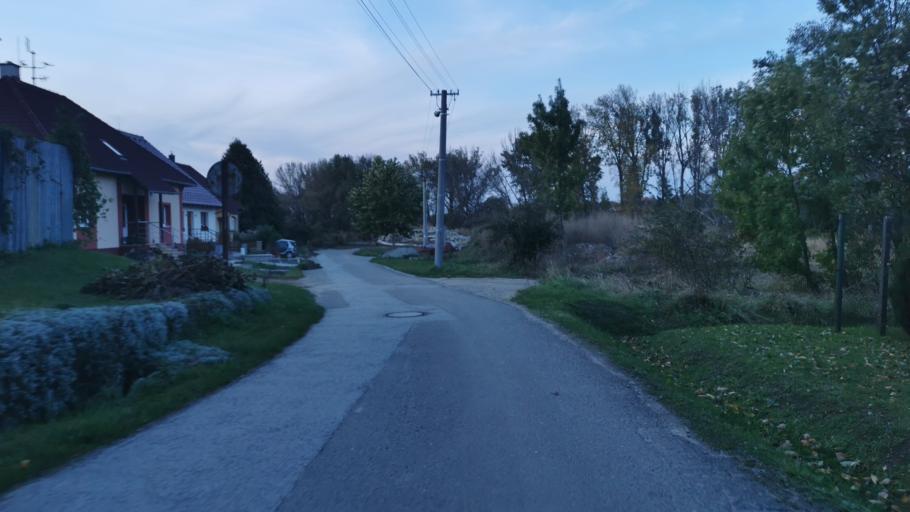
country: SK
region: Trnavsky
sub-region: Okres Skalica
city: Skalica
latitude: 48.8142
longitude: 17.2414
